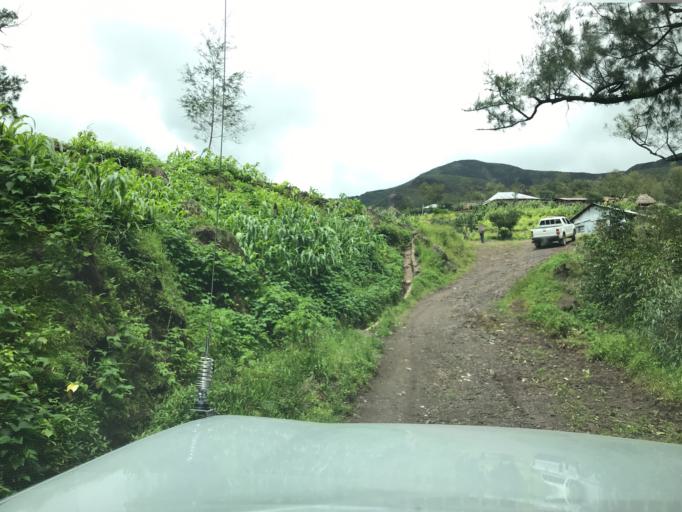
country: TL
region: Aileu
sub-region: Aileu Villa
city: Aileu
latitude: -8.8637
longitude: 125.5611
